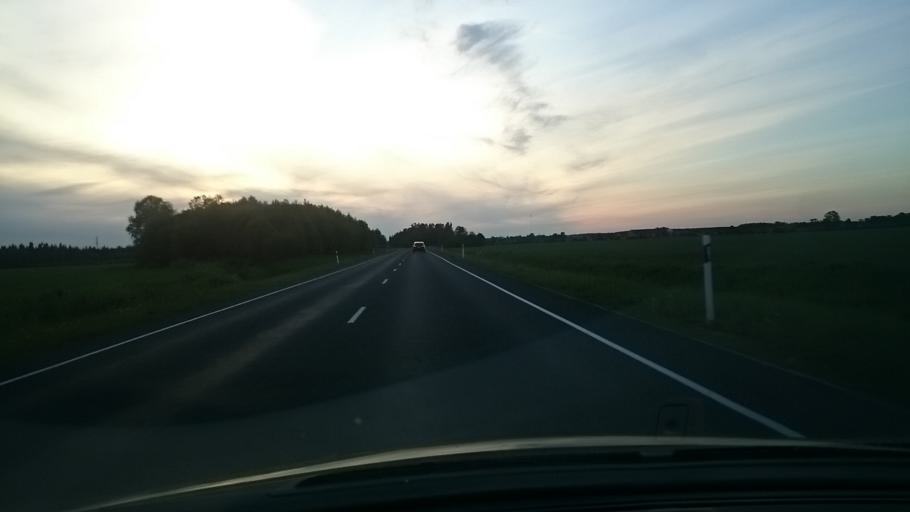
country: EE
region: Viljandimaa
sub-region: Vohma linn
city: Vohma
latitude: 58.7334
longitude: 25.5913
